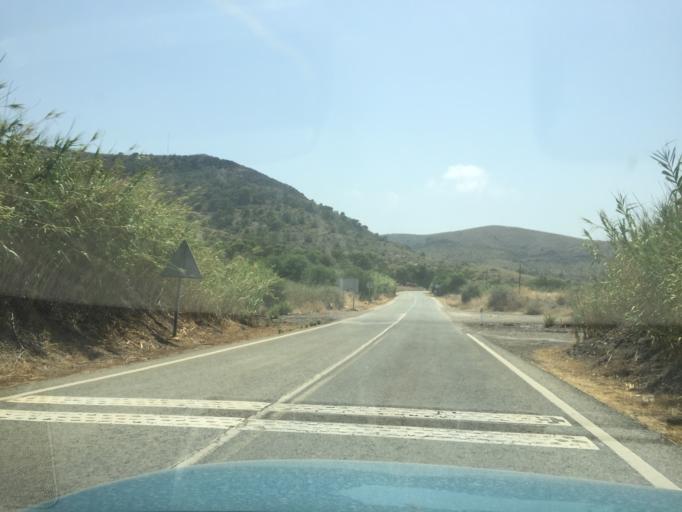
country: ES
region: Murcia
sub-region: Murcia
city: La Union
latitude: 37.5898
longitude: -0.8568
